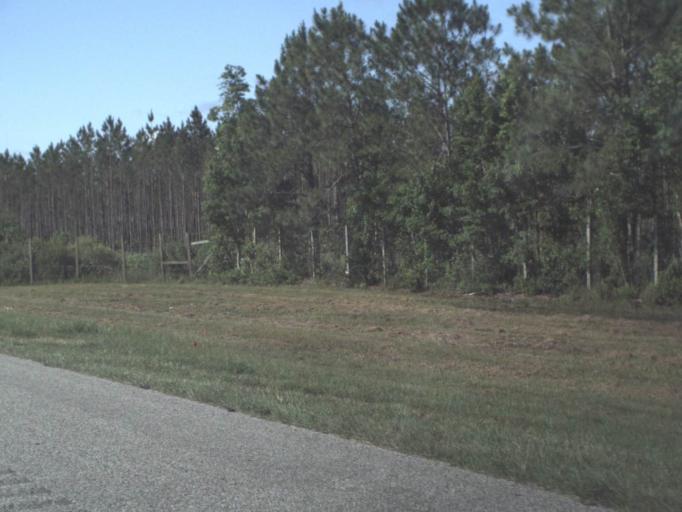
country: US
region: Florida
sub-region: Saint Johns County
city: Saint Augustine Shores
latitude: 29.7610
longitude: -81.3520
